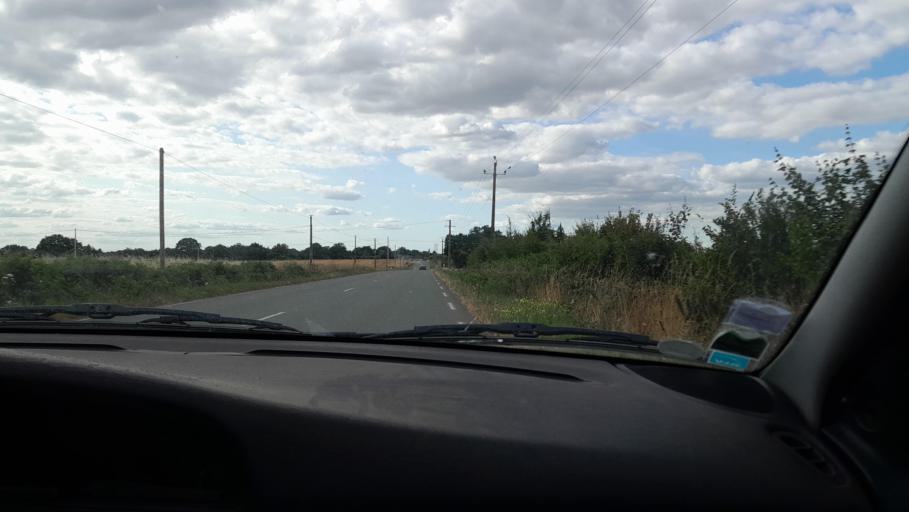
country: FR
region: Pays de la Loire
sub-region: Departement de la Mayenne
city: Ballots
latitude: 47.9279
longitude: -1.0735
